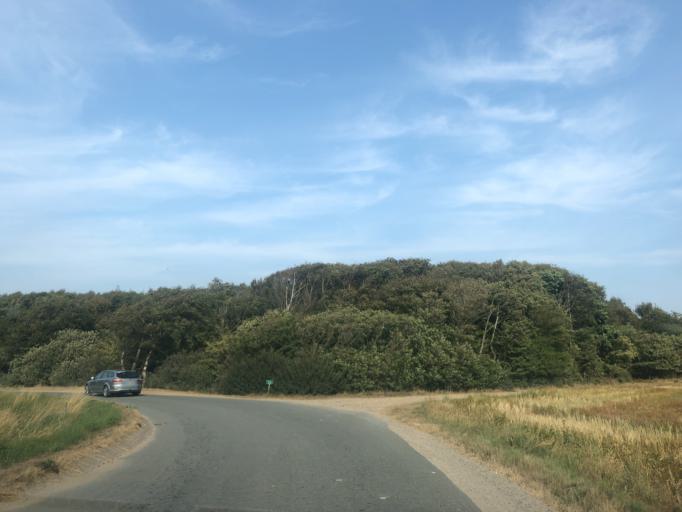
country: DK
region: North Denmark
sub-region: Morso Kommune
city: Nykobing Mors
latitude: 56.8336
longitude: 9.0444
